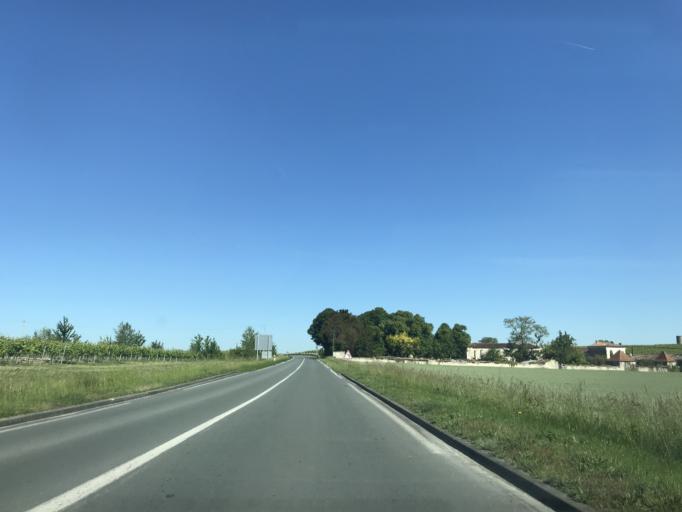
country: FR
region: Poitou-Charentes
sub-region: Departement de la Charente
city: Segonzac
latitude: 45.5292
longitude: -0.3059
